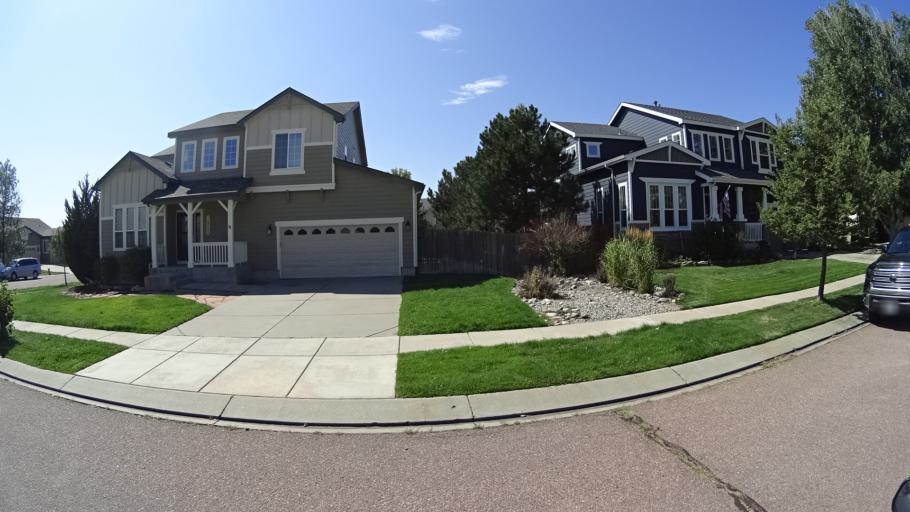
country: US
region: Colorado
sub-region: El Paso County
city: Cimarron Hills
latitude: 38.9199
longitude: -104.6976
